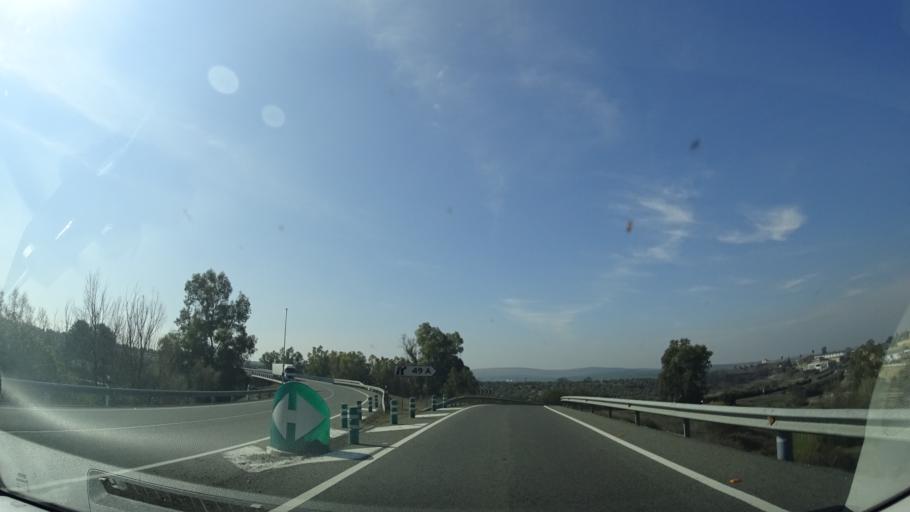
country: ES
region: Andalusia
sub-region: Province of Cordoba
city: Montoro
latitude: 38.0117
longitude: -4.3715
